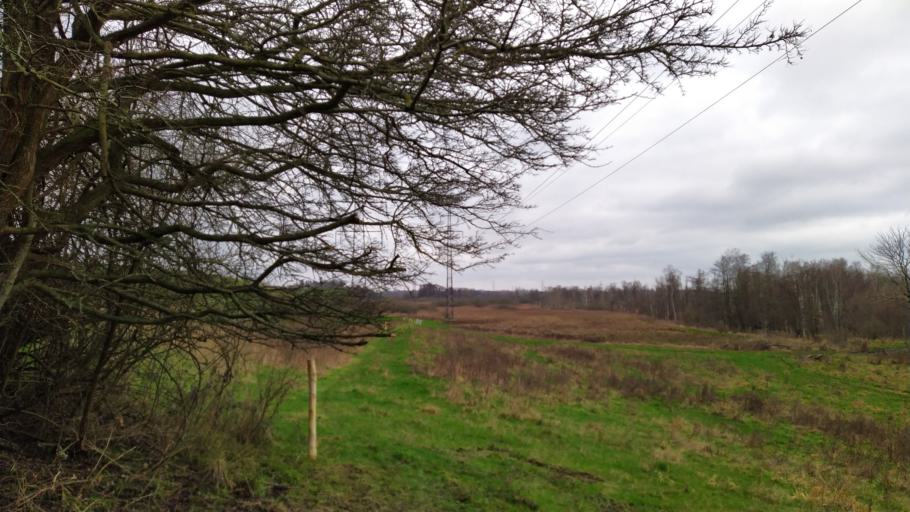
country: DK
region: Capital Region
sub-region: Egedal Kommune
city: Stenlose
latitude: 55.7612
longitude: 12.2121
